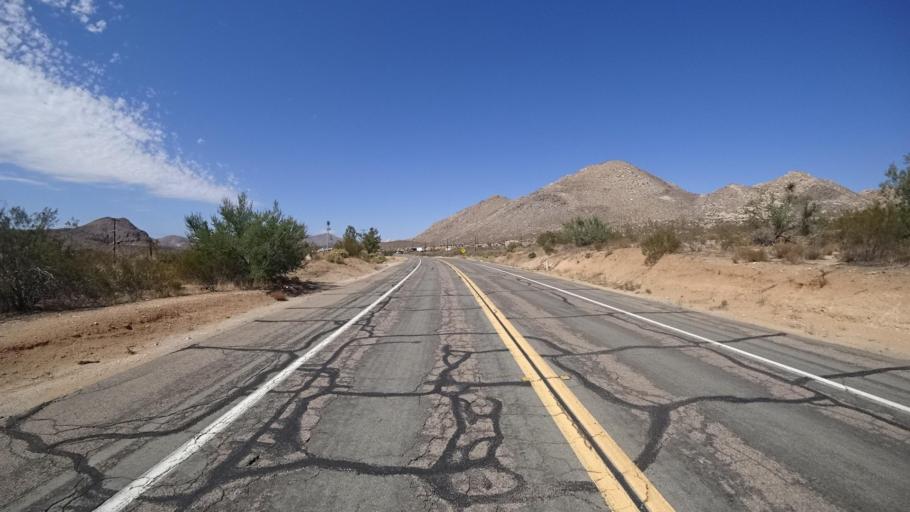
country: MX
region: Baja California
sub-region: Tecate
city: Cereso del Hongo
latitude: 32.6323
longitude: -116.1644
